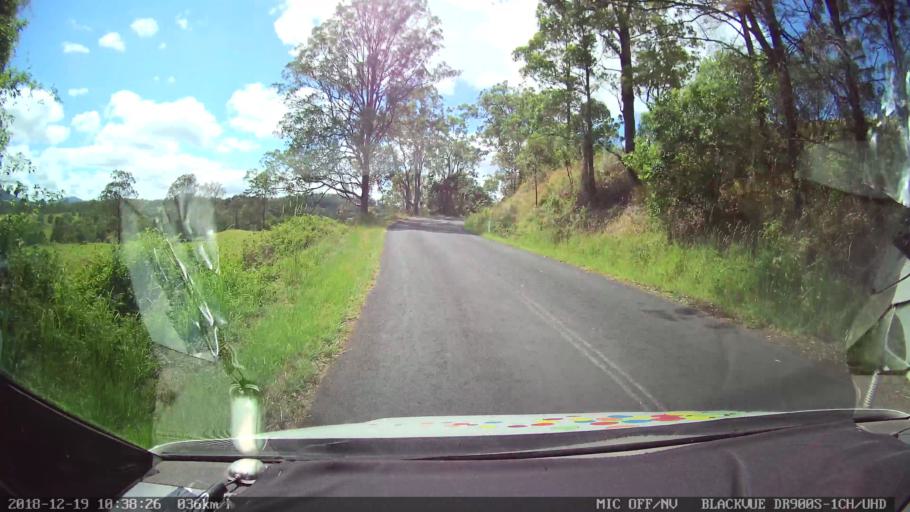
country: AU
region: New South Wales
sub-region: Lismore Municipality
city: Nimbin
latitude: -28.5751
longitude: 153.1543
